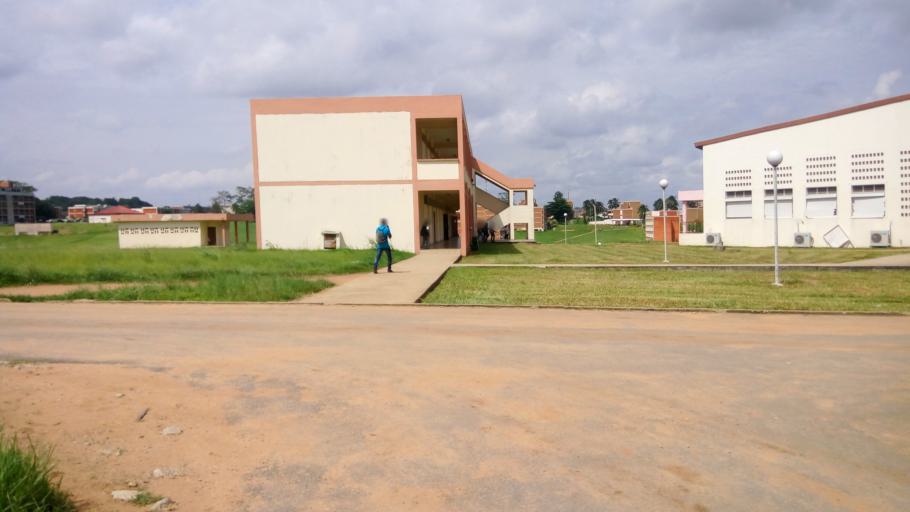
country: CI
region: Lagunes
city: Abidjan
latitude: 5.3419
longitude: -3.9929
